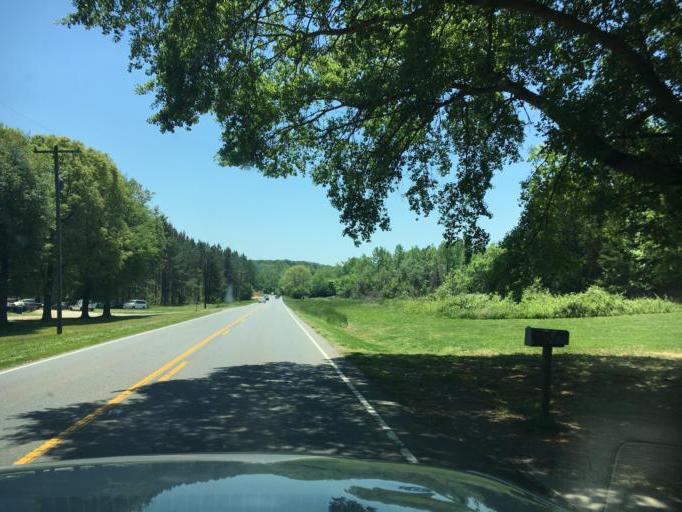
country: US
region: South Carolina
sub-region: Cherokee County
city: Blacksburg
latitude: 35.1900
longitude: -81.5680
